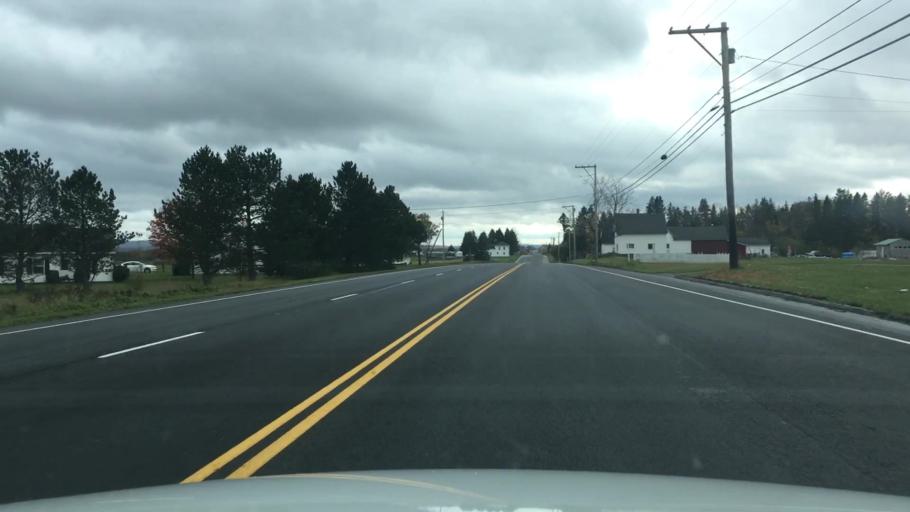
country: US
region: Maine
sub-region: Aroostook County
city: Houlton
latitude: 46.2268
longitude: -67.8410
